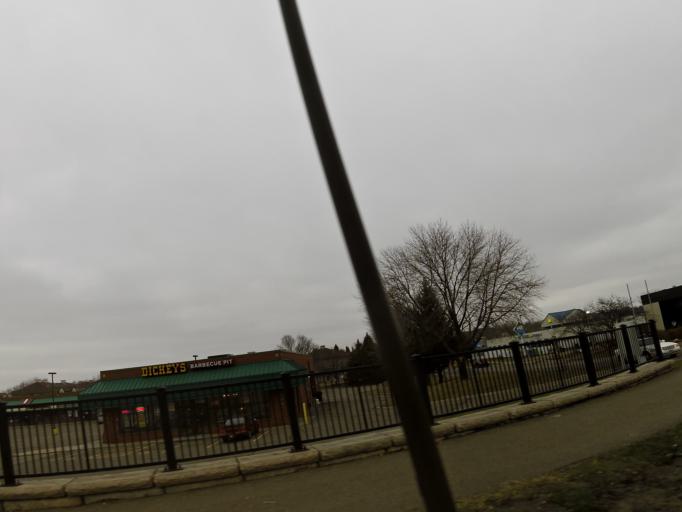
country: US
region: Minnesota
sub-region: Scott County
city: Savage
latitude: 44.7466
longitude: -93.3309
